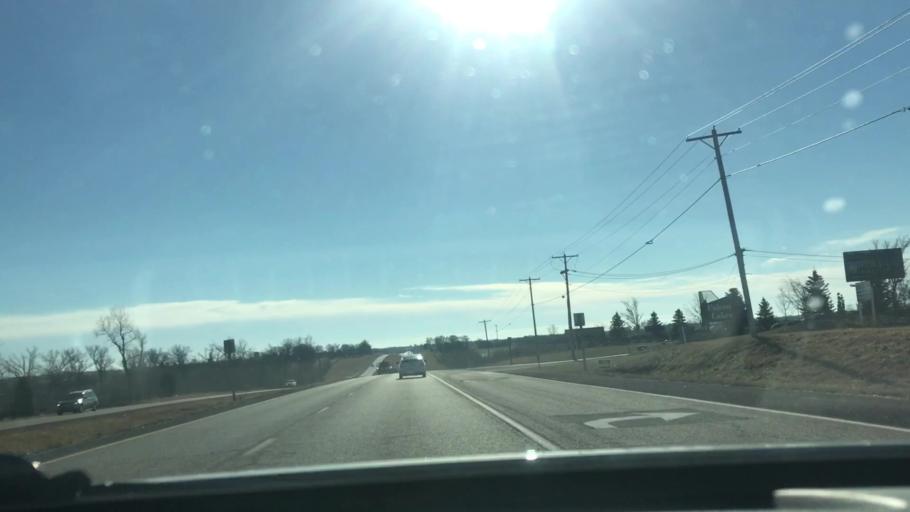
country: US
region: Kansas
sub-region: Leavenworth County
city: Basehor
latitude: 39.1689
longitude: -94.9009
